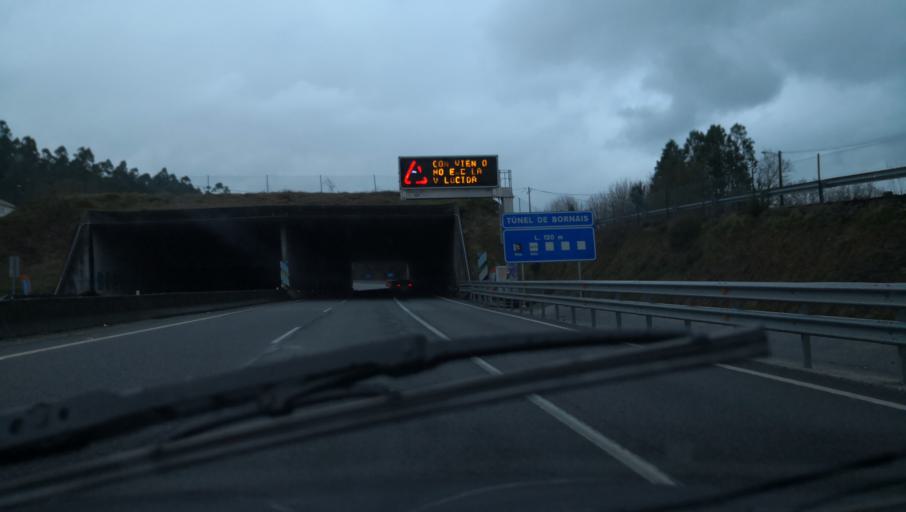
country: ES
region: Galicia
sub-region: Provincia da Coruna
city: Santiago de Compostela
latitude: 42.8401
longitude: -8.5291
